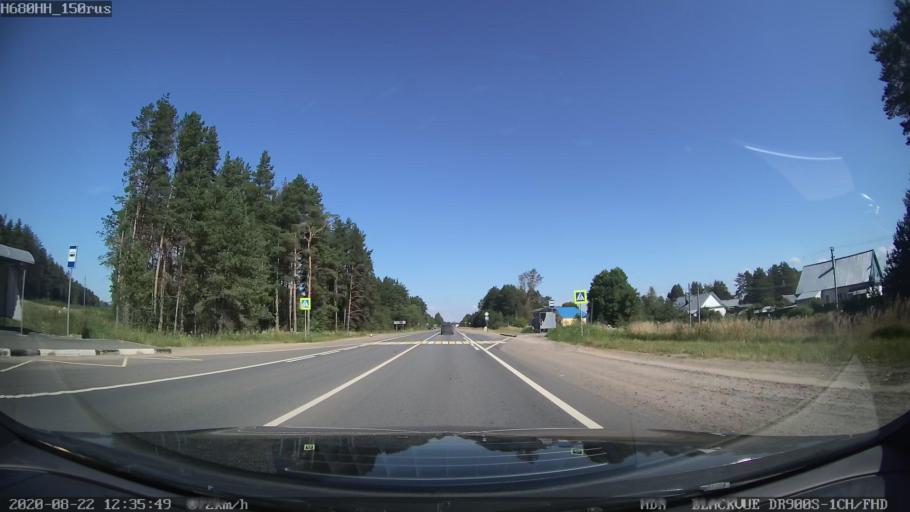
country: RU
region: Tverskaya
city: Rameshki
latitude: 57.2761
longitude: 36.0747
